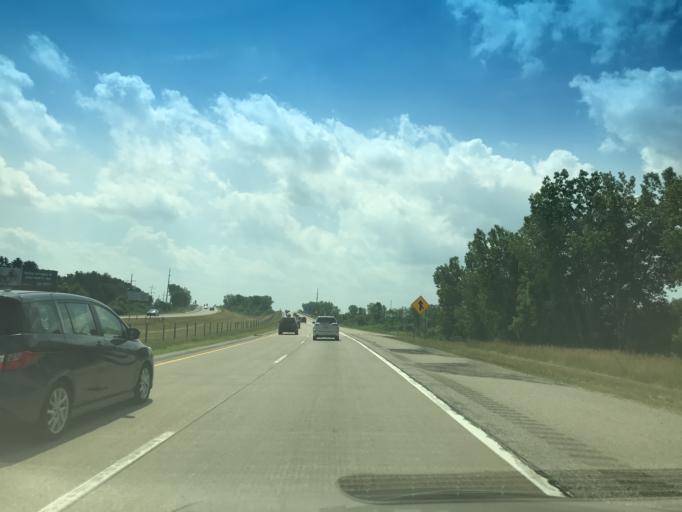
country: US
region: Michigan
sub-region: Eaton County
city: Dimondale
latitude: 42.6879
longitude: -84.6664
